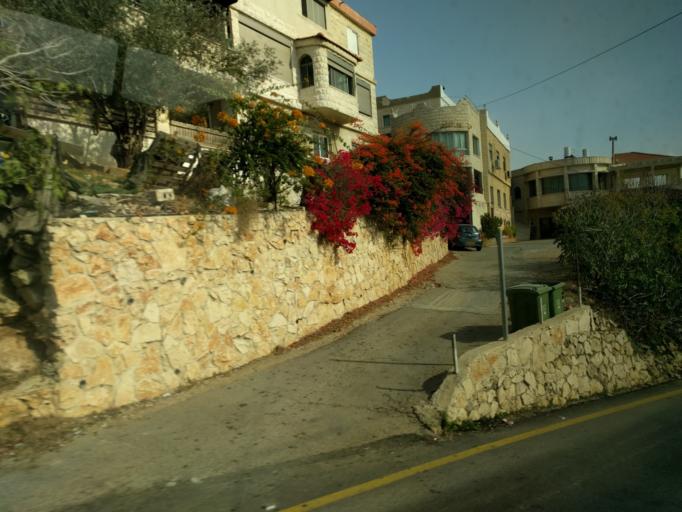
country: IL
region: Haifa
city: Daliyat el Karmil
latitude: 32.7148
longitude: 35.0690
